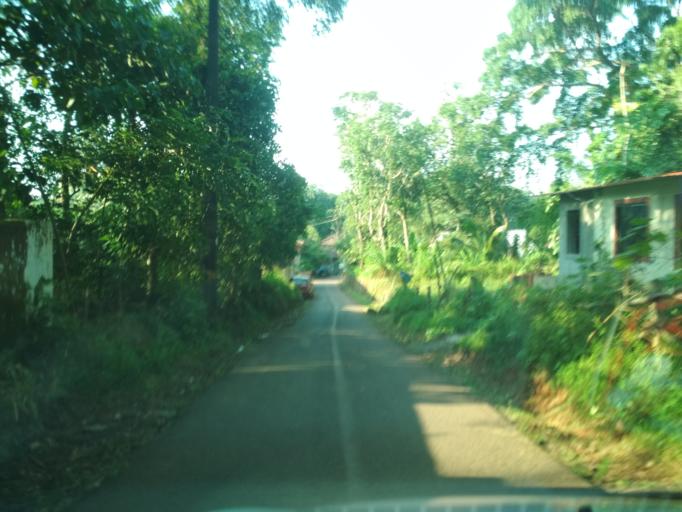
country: IN
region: Goa
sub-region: North Goa
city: Serula
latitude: 15.5474
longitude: 73.8207
